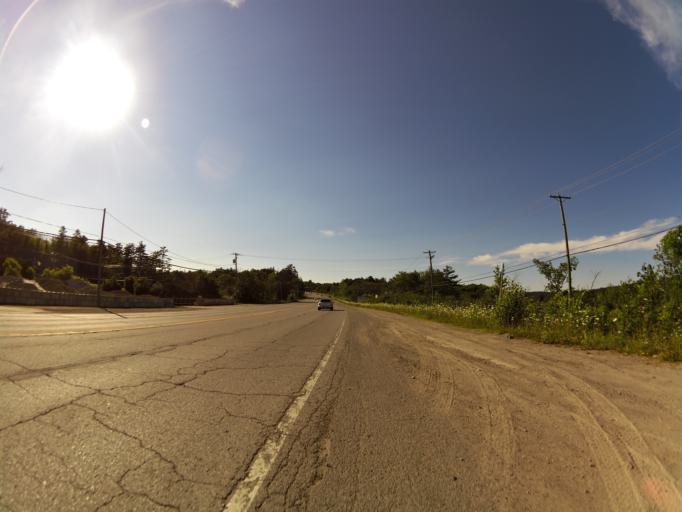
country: CA
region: Quebec
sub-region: Outaouais
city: Gatineau
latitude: 45.4798
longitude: -75.7453
